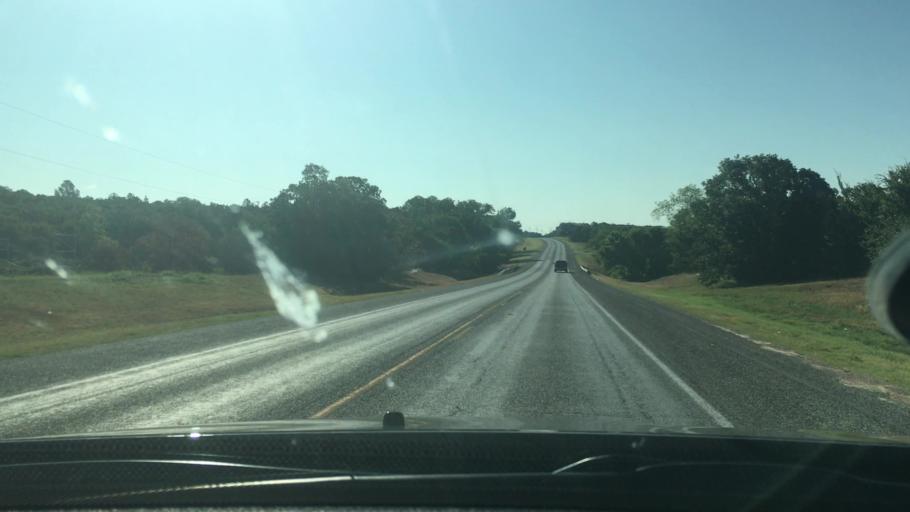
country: US
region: Oklahoma
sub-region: Johnston County
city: Tishomingo
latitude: 34.2398
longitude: -96.7405
